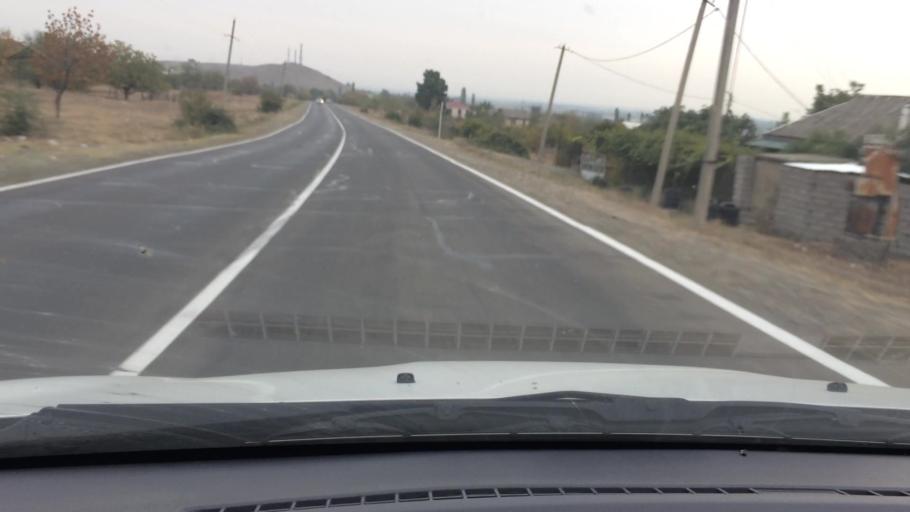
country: GE
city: Naghvarevi
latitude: 41.3547
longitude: 44.8264
